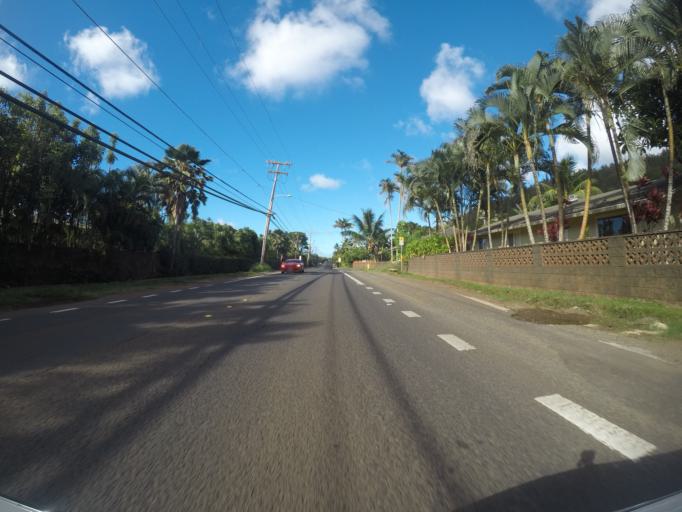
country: US
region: Hawaii
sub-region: Honolulu County
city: Pupukea
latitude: 21.6803
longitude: -158.0334
